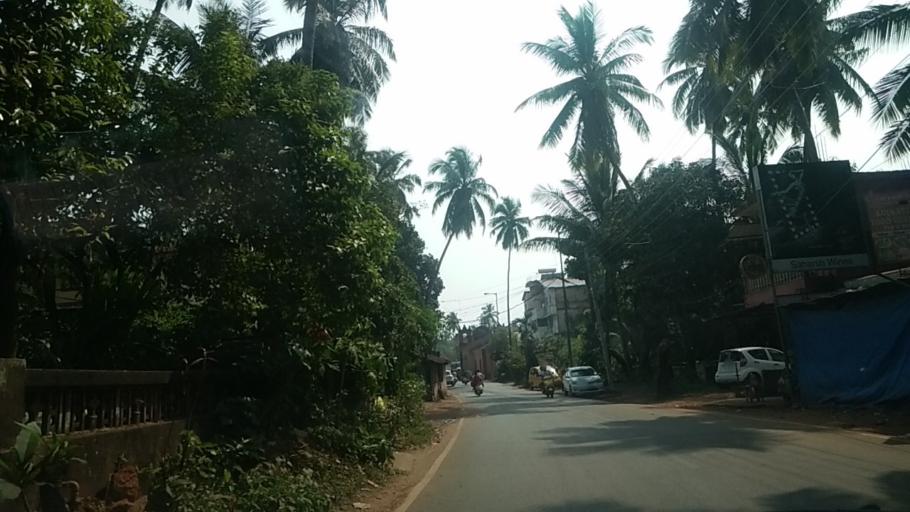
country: IN
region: Goa
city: Calangute
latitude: 15.5470
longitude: 73.7645
